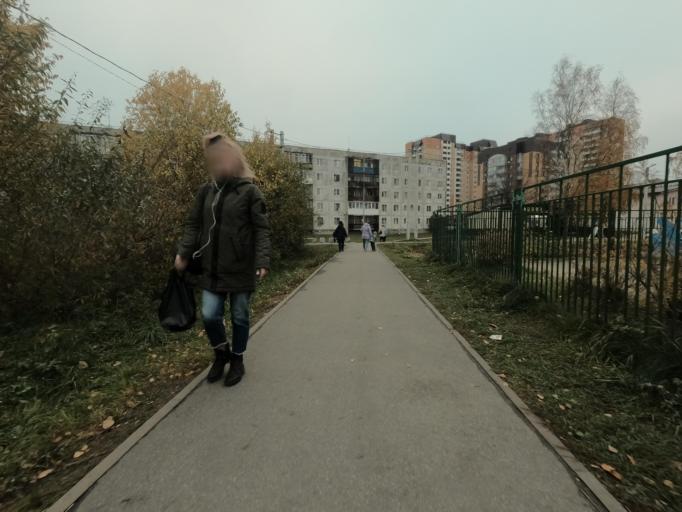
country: RU
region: Leningrad
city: Kirovsk
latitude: 59.8830
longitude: 30.9940
